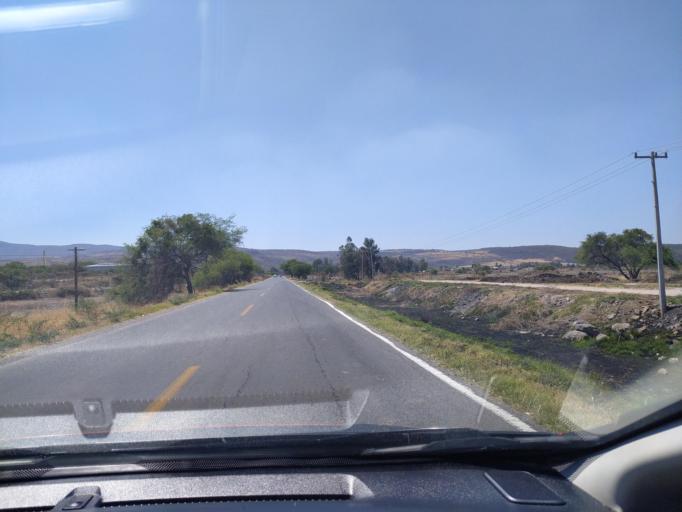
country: MX
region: Guanajuato
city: Ciudad Manuel Doblado
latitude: 20.7404
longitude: -101.9431
